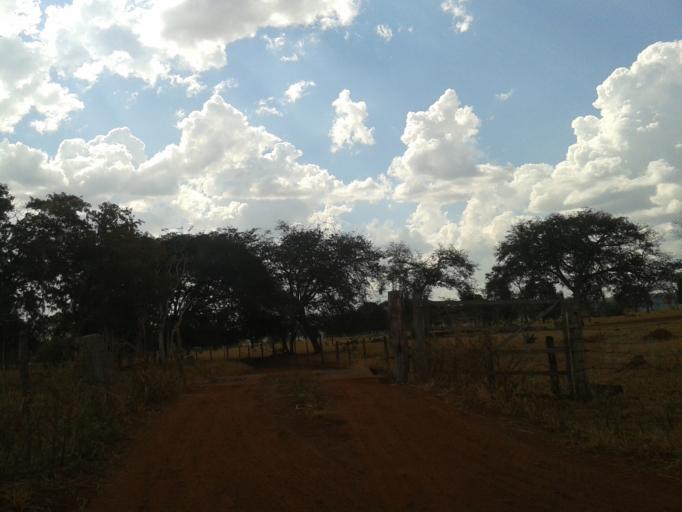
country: BR
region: Minas Gerais
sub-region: Santa Vitoria
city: Santa Vitoria
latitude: -19.1943
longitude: -49.9735
